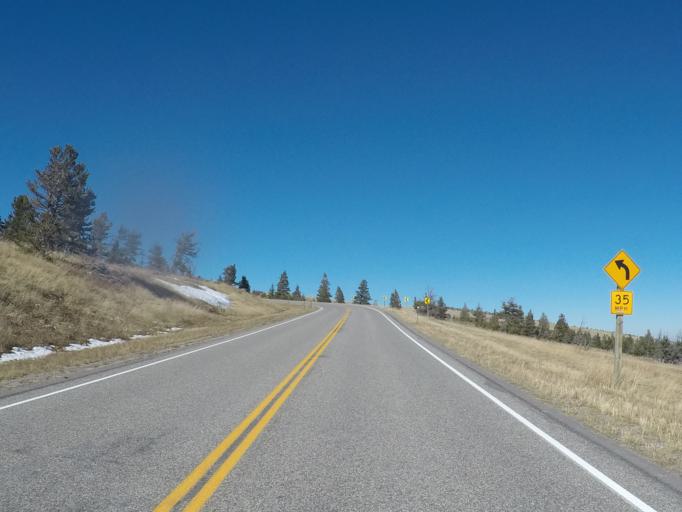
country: US
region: Wyoming
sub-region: Park County
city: Cody
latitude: 44.7171
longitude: -109.3285
